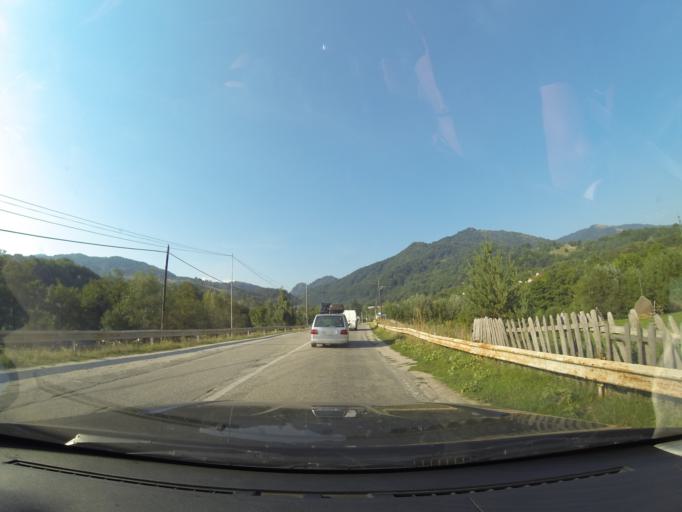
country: RO
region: Arges
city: Poenari
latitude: 45.3330
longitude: 24.6357
